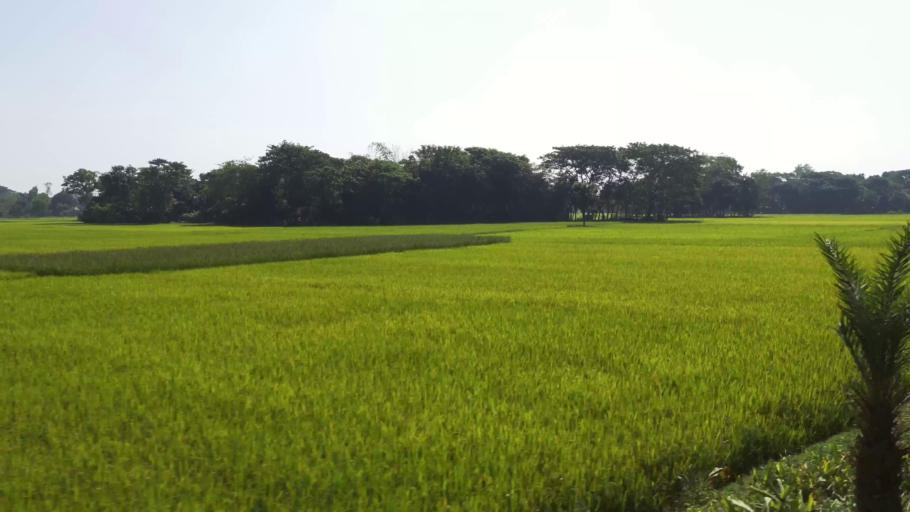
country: BD
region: Dhaka
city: Gafargaon
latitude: 24.5069
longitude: 90.5168
